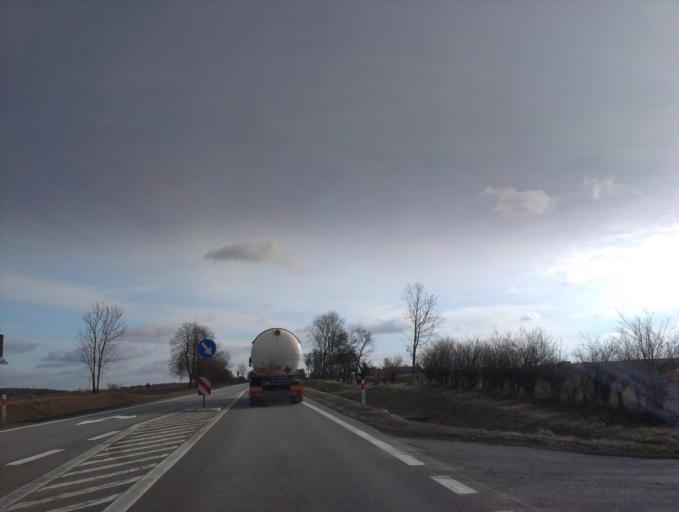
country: PL
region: Kujawsko-Pomorskie
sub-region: Powiat lipnowski
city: Kikol
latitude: 52.8857
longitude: 19.1330
